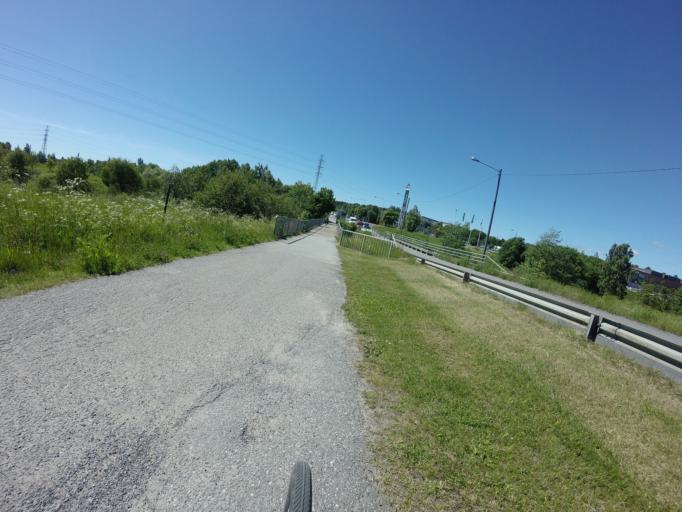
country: FI
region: Varsinais-Suomi
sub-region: Turku
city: Turku
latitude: 60.4728
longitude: 22.2900
